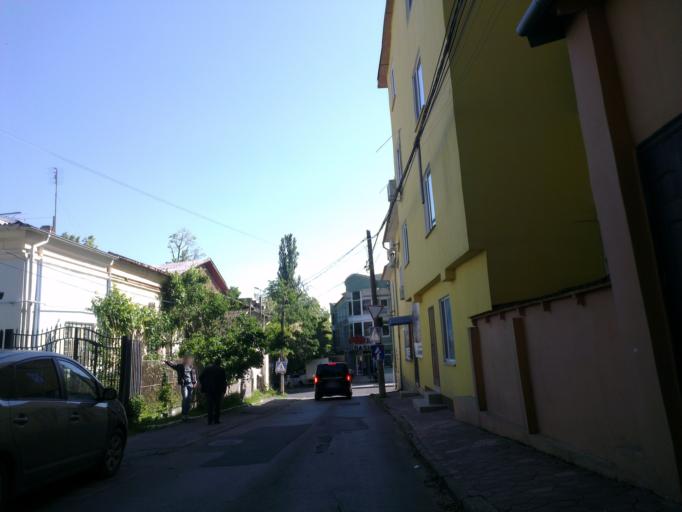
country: MD
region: Chisinau
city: Chisinau
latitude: 47.0146
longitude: 28.8266
